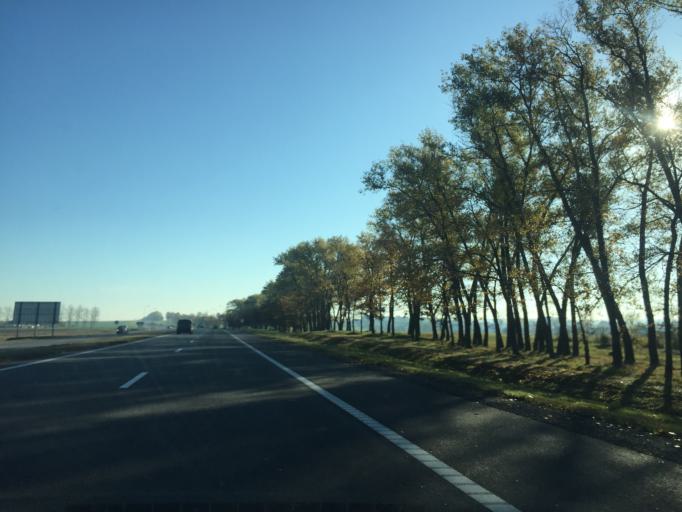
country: BY
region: Minsk
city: Smilavichy
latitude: 53.7593
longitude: 28.0252
